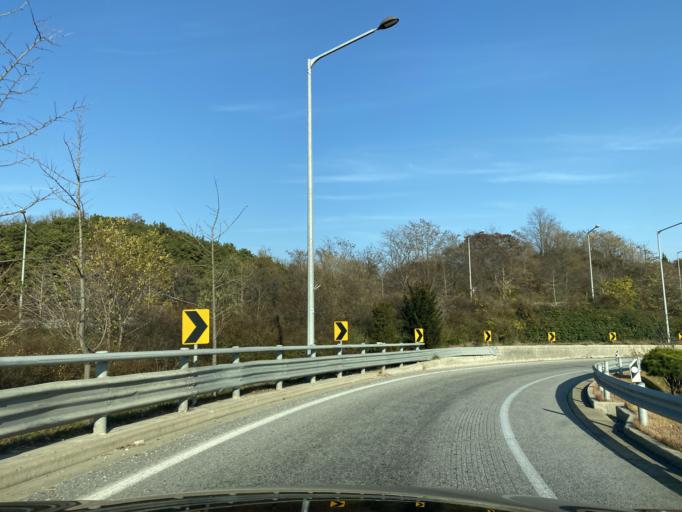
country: KR
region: Chungcheongnam-do
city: Asan
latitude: 36.7810
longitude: 126.9389
